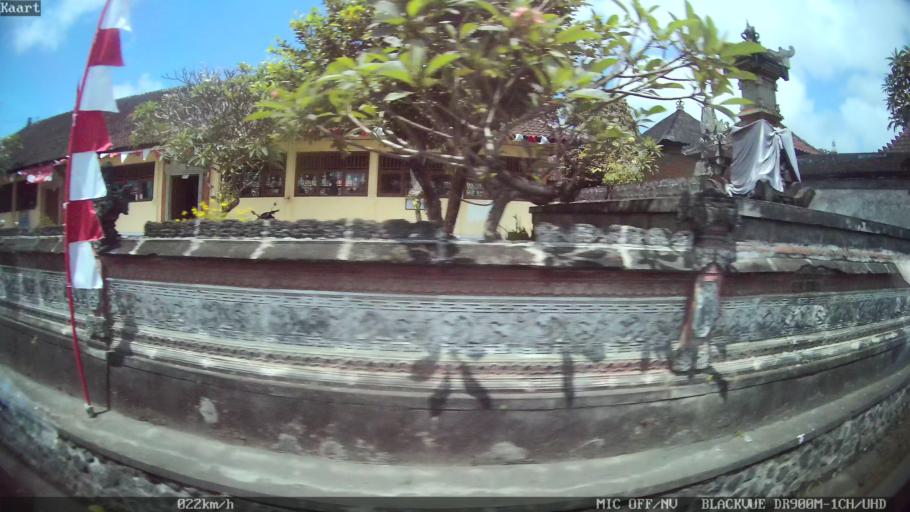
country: ID
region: Bali
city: Banjar Pasekan
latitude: -8.5912
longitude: 115.2856
